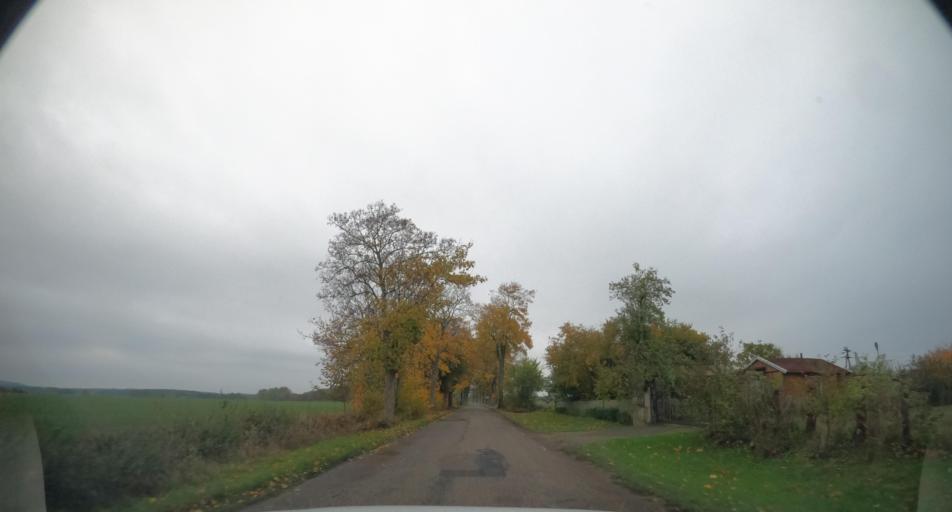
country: PL
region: West Pomeranian Voivodeship
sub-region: Powiat kamienski
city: Wolin
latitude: 53.9160
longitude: 14.6113
